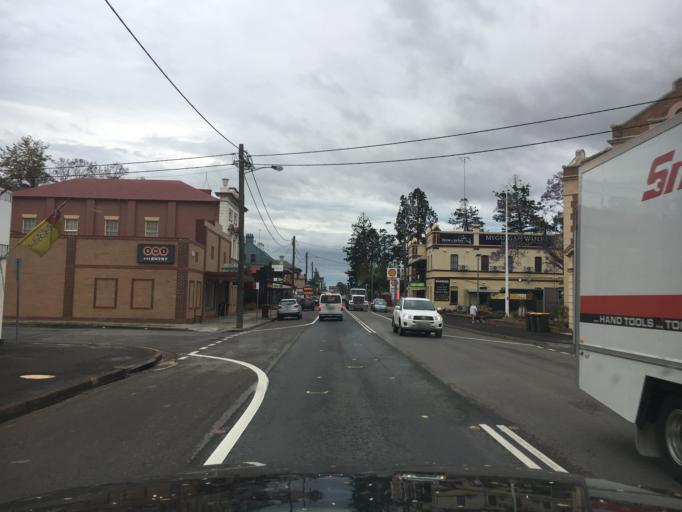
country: AU
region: New South Wales
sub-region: Singleton
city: Singleton
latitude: -32.5619
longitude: 151.1752
